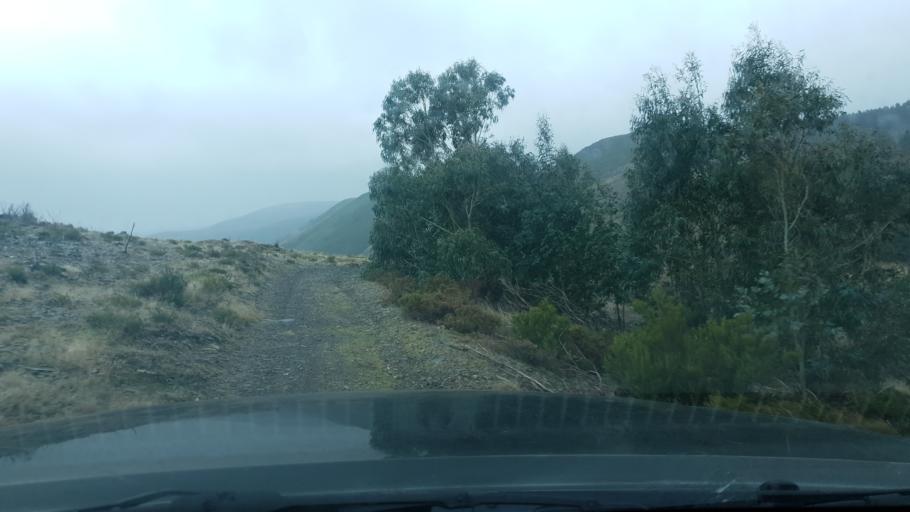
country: PT
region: Viseu
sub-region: Sao Pedro do Sul
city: Sao Pedro do Sul
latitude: 40.8577
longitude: -8.0986
